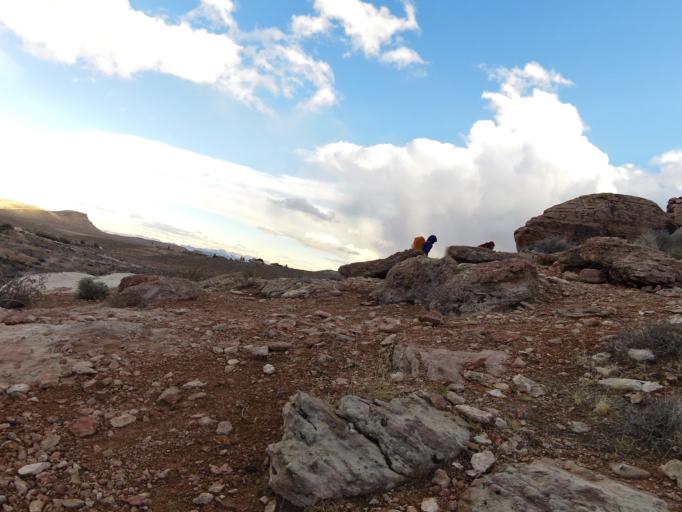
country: US
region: Nevada
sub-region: Clark County
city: Summerlin South
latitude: 36.1499
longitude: -115.4231
